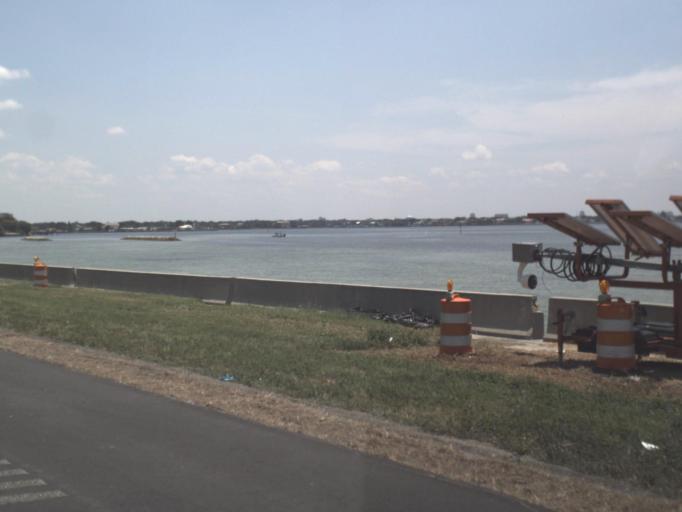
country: US
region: Florida
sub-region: Hillsborough County
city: Town 'n' Country
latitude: 27.9404
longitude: -82.5514
